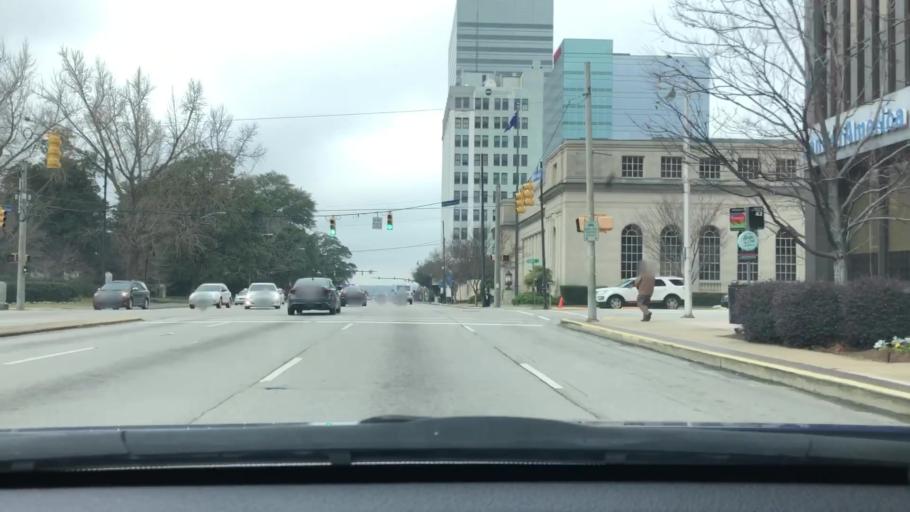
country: US
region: South Carolina
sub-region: Richland County
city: Columbia
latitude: 34.0019
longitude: -81.0316
